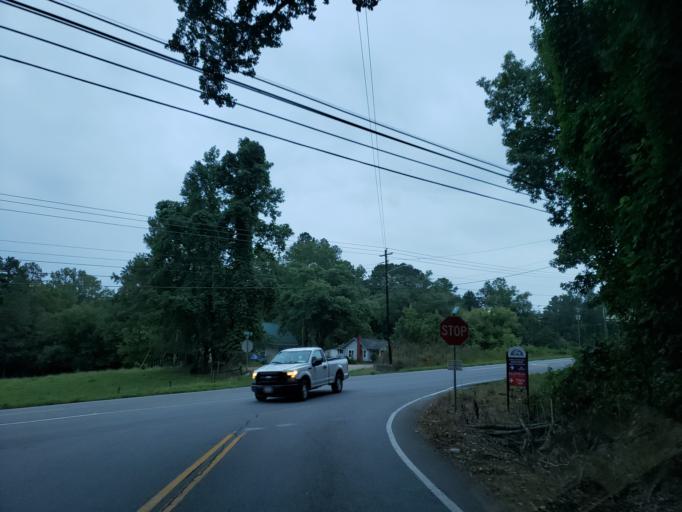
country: US
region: Georgia
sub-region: Cherokee County
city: Canton
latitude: 34.2765
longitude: -84.4497
